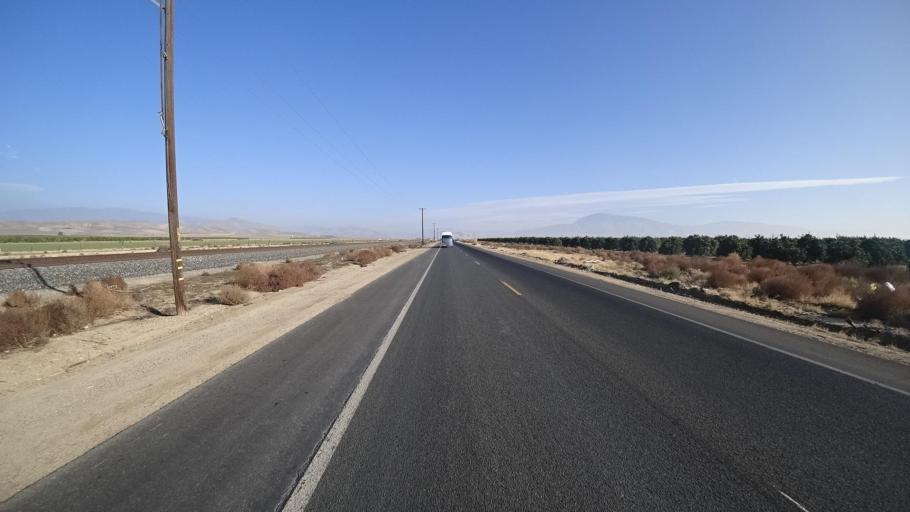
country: US
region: California
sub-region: Kern County
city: Lamont
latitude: 35.3383
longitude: -118.8309
